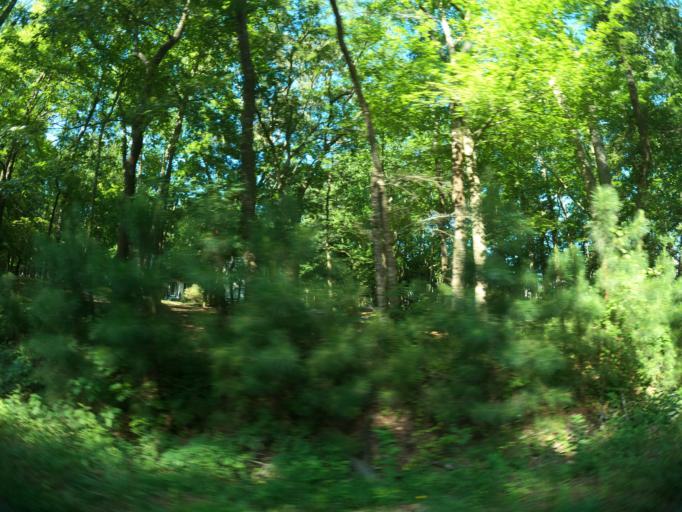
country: US
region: Delaware
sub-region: Sussex County
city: Ocean View
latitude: 38.4807
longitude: -75.1181
